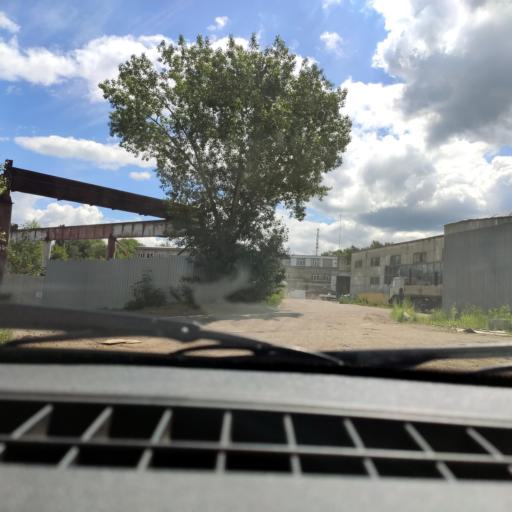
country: RU
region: Bashkortostan
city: Ufa
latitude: 54.8380
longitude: 56.1144
